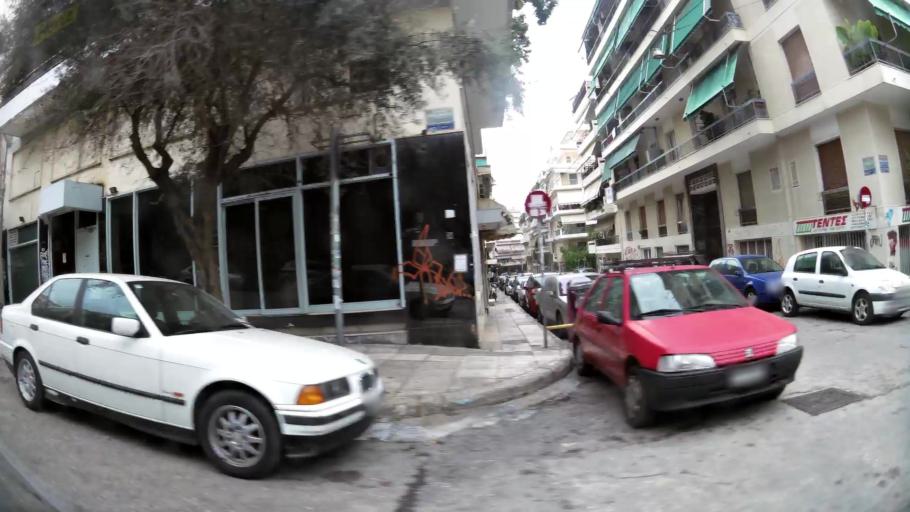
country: GR
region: Attica
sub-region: Nomarchia Athinas
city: Vyronas
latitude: 37.9649
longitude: 23.7440
